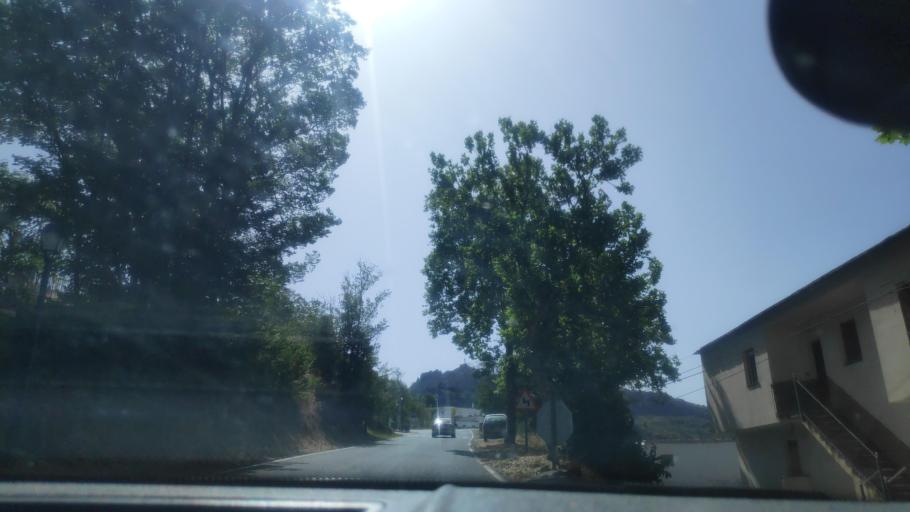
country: ES
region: Andalusia
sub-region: Provincia de Granada
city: Busquistar
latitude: 36.9386
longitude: -3.2937
